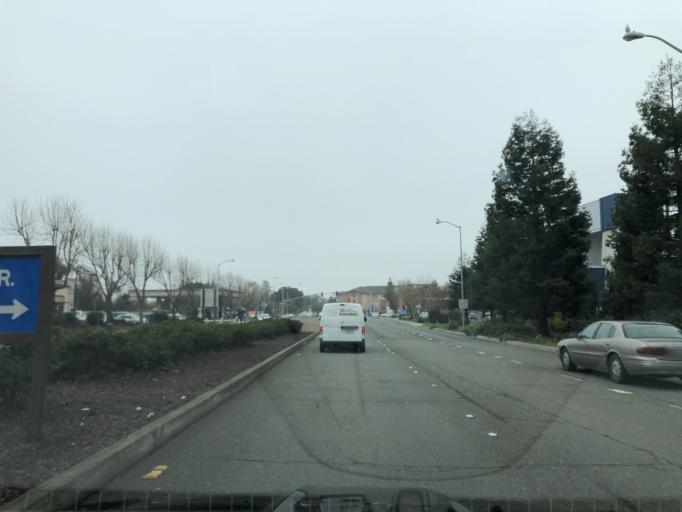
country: US
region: California
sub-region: Alameda County
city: Union City
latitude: 37.5984
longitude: -122.0645
